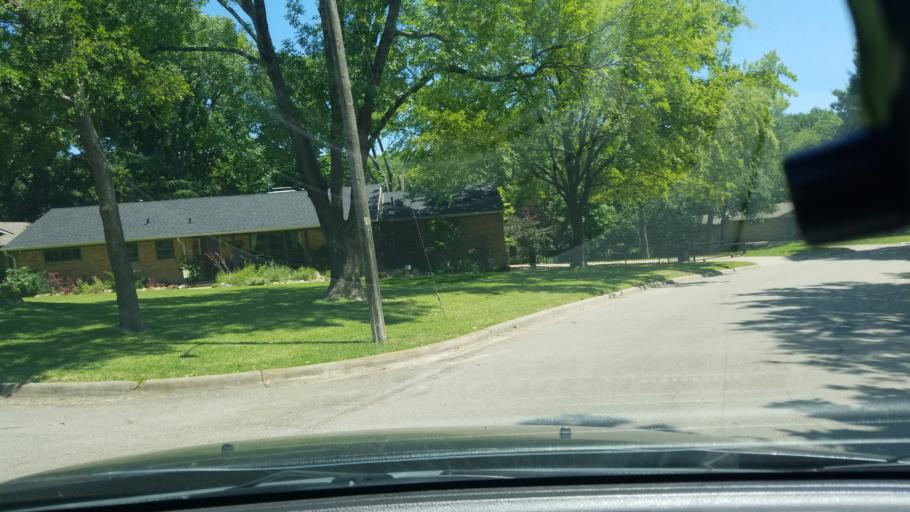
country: US
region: Texas
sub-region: Dallas County
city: Mesquite
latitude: 32.7530
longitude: -96.6043
